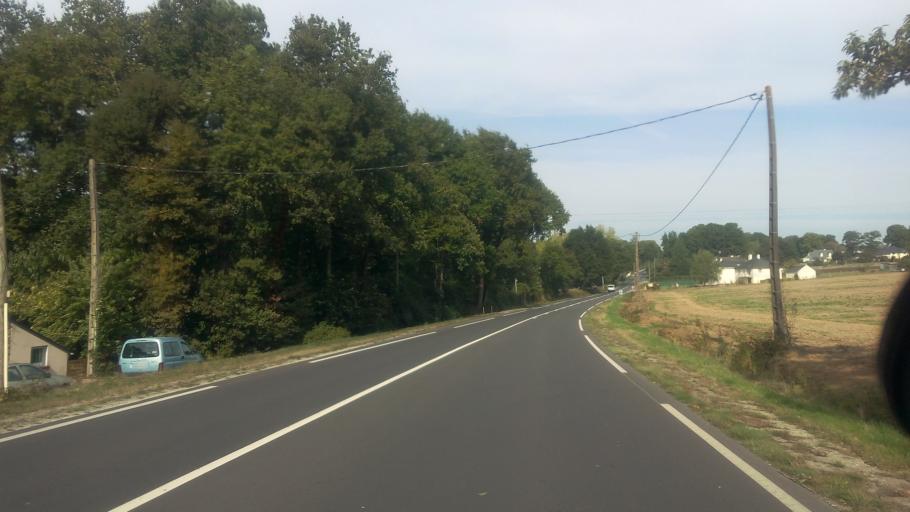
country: FR
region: Brittany
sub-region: Departement d'Ille-et-Vilaine
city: Bains-sur-Oust
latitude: 47.6845
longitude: -2.0865
